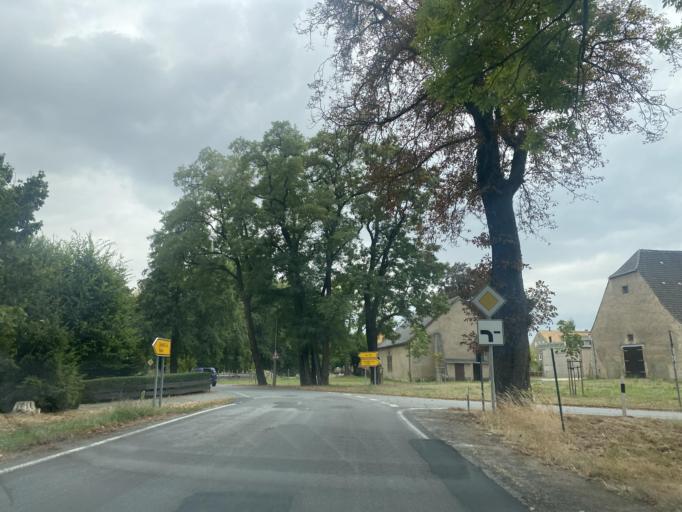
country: DE
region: Saxony
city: Neschwitz
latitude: 51.2727
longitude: 14.3262
